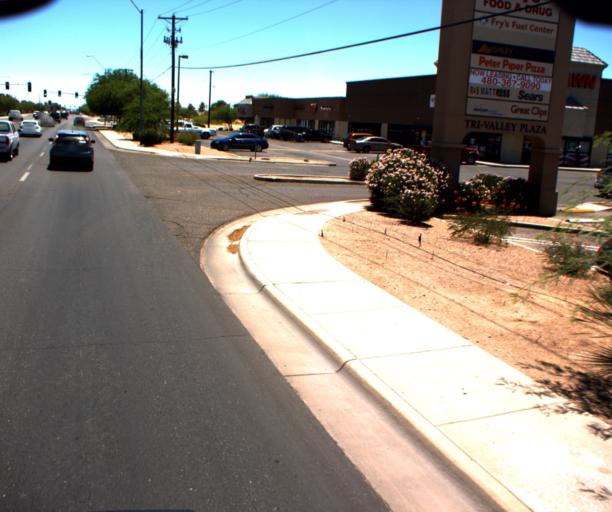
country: US
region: Arizona
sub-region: Pinal County
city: Casa Grande
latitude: 32.8795
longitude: -111.7285
